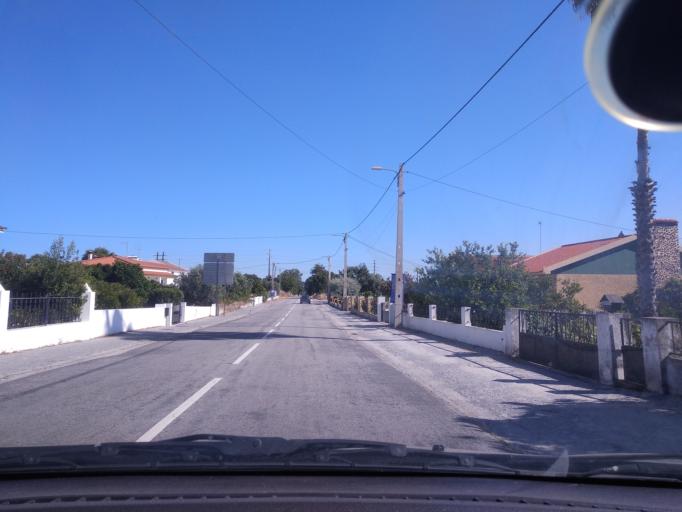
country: PT
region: Portalegre
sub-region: Nisa
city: Nisa
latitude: 39.4222
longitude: -7.6199
